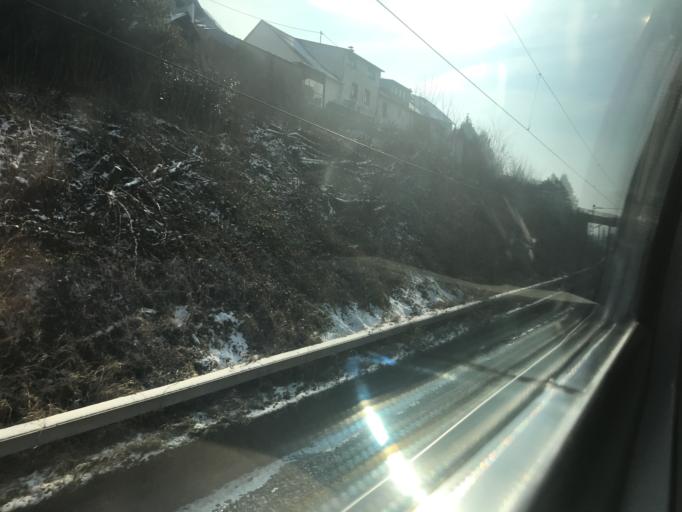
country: DE
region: Rheinland-Pfalz
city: Fohren
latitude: 49.8617
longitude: 6.7698
